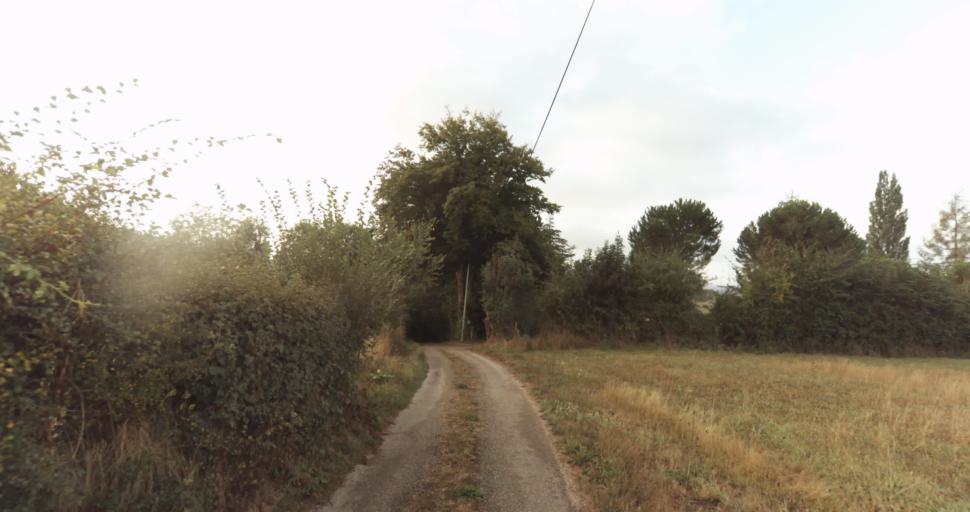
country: FR
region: Lower Normandy
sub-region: Departement de l'Orne
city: Vimoutiers
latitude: 48.9191
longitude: 0.2203
